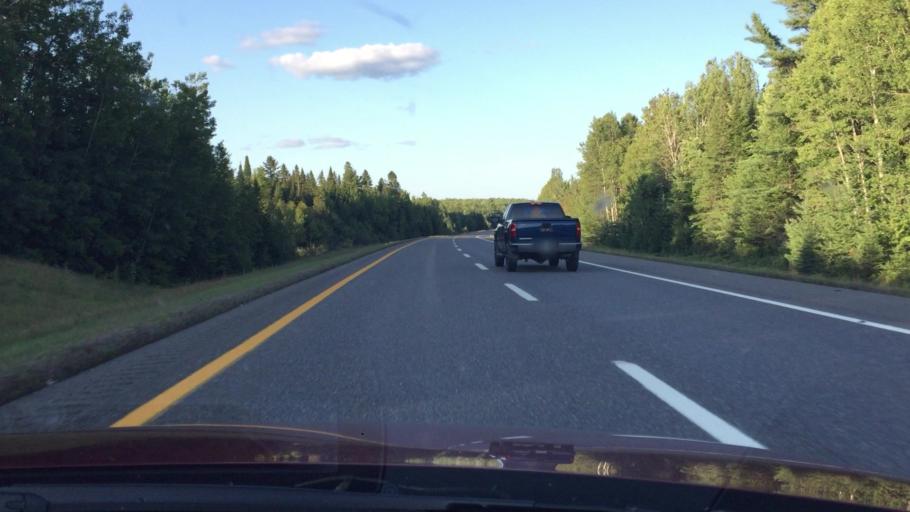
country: US
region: Maine
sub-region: Penobscot County
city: Patten
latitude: 46.0406
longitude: -68.2631
